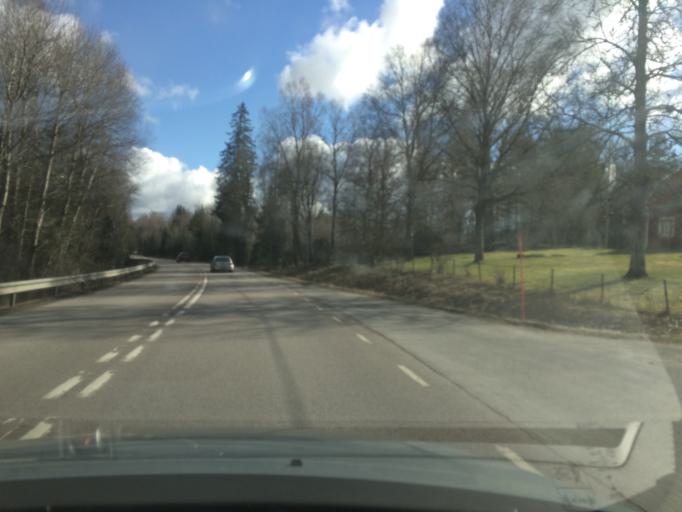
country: SE
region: Vaestra Goetaland
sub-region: Skara Kommun
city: Skara
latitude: 58.3175
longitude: 13.4350
